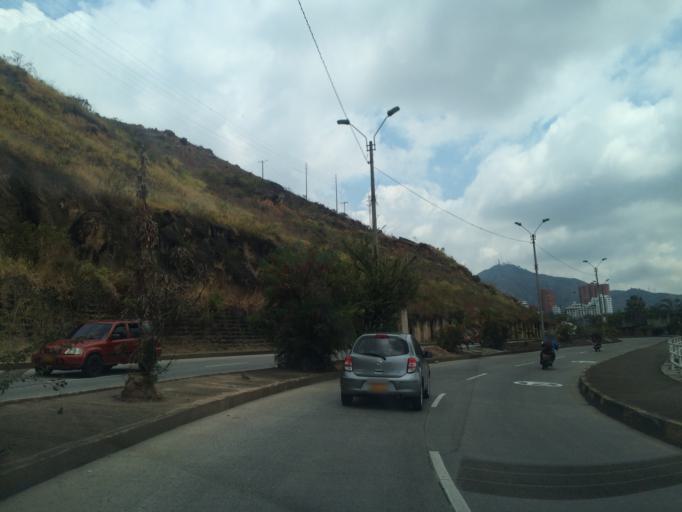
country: CO
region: Valle del Cauca
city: Cali
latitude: 3.4368
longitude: -76.5492
